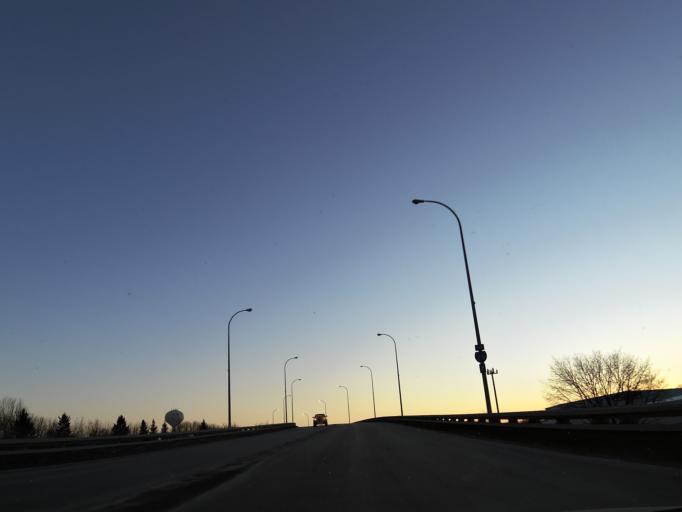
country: US
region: North Dakota
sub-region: Grand Forks County
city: Grand Forks
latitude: 47.9209
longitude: -97.0369
